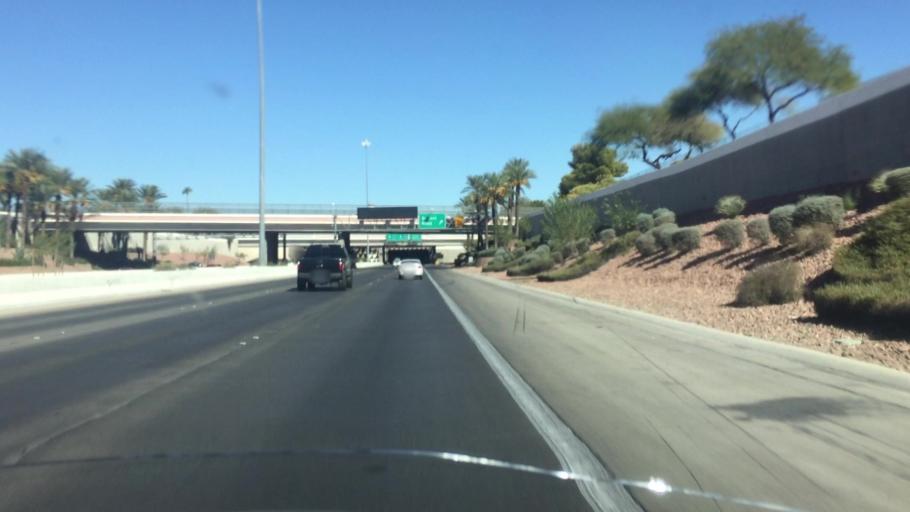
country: US
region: Nevada
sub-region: Clark County
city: Paradise
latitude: 36.0686
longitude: -115.1471
